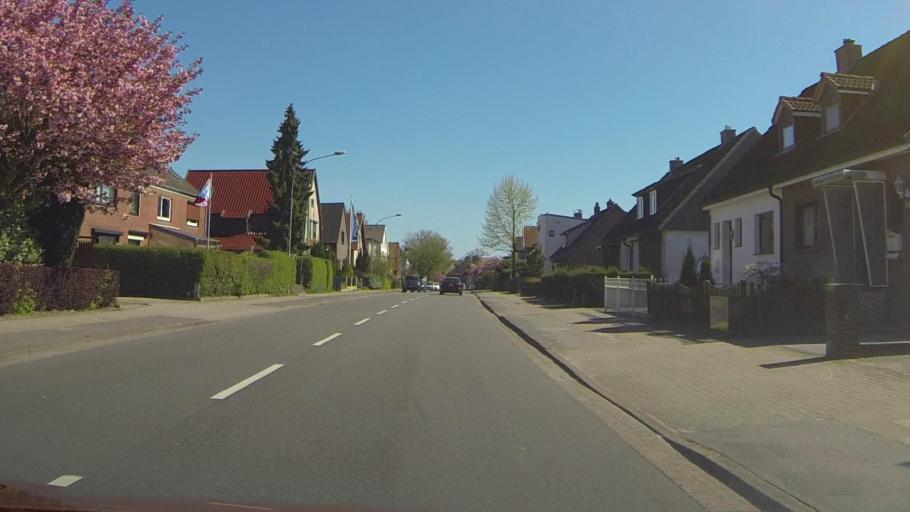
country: DE
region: Schleswig-Holstein
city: Pinneberg
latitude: 53.6673
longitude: 9.7869
